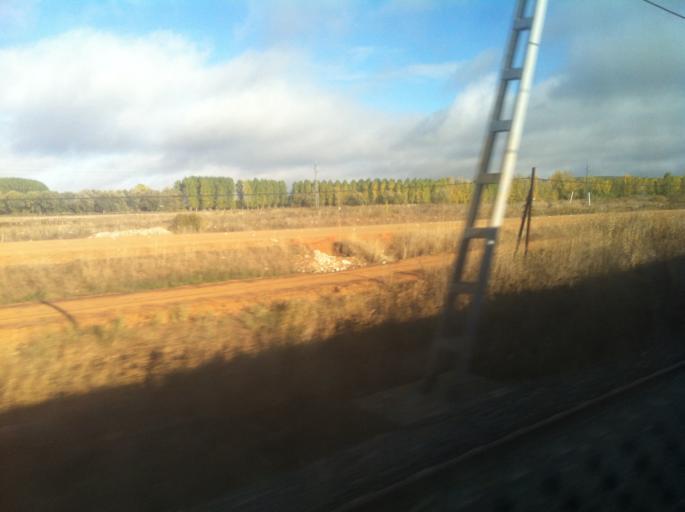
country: ES
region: Castille and Leon
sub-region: Provincia de Burgos
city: Buniel
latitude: 42.3253
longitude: -3.8142
